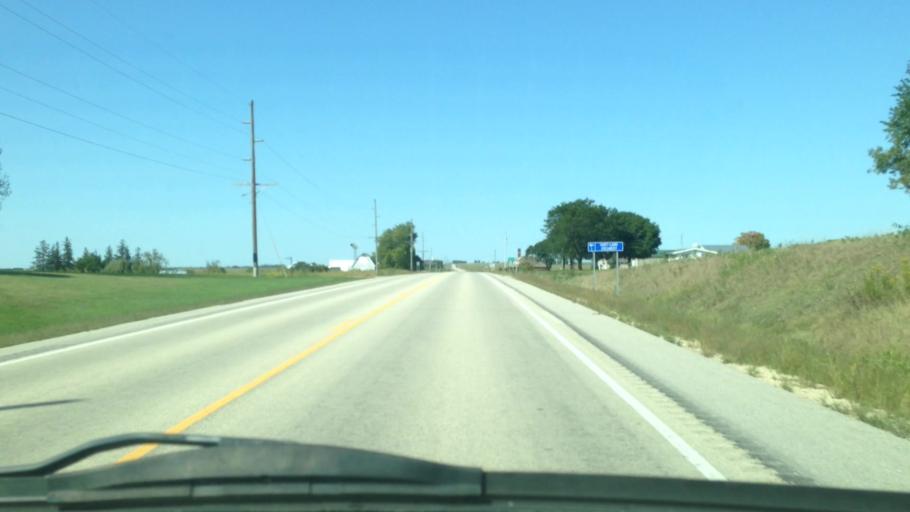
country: US
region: Minnesota
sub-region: Fillmore County
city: Rushford
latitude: 43.8719
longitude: -91.7396
